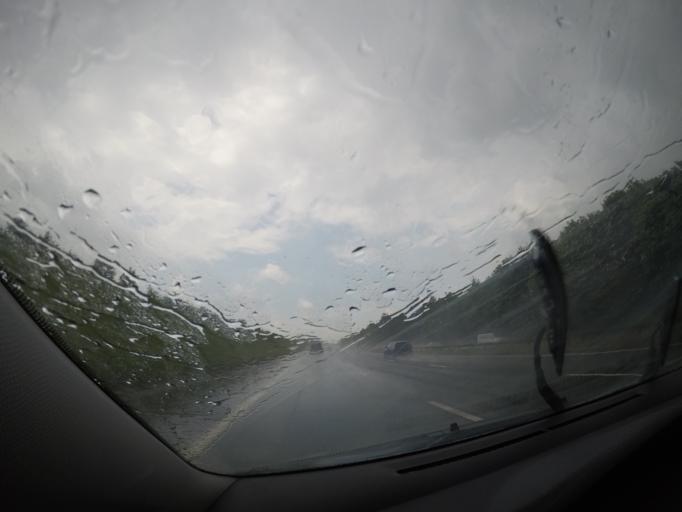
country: GB
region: England
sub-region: Cumbria
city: Penrith
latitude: 54.7179
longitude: -2.7984
